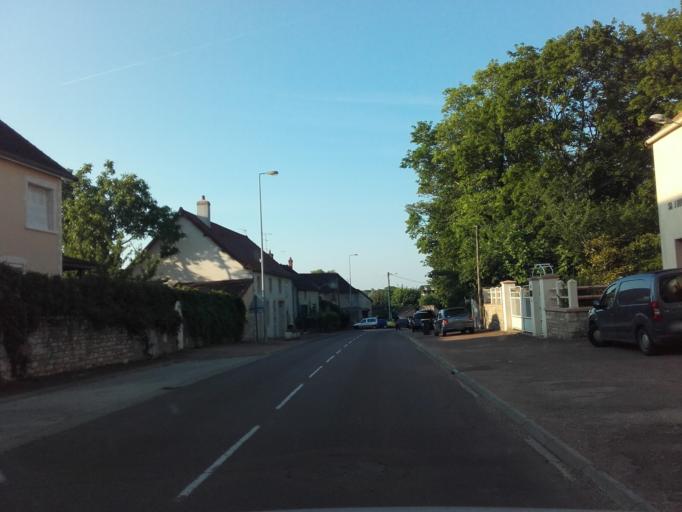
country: FR
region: Bourgogne
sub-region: Departement de Saone-et-Loire
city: Dracy-le-Fort
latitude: 46.8098
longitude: 4.7533
